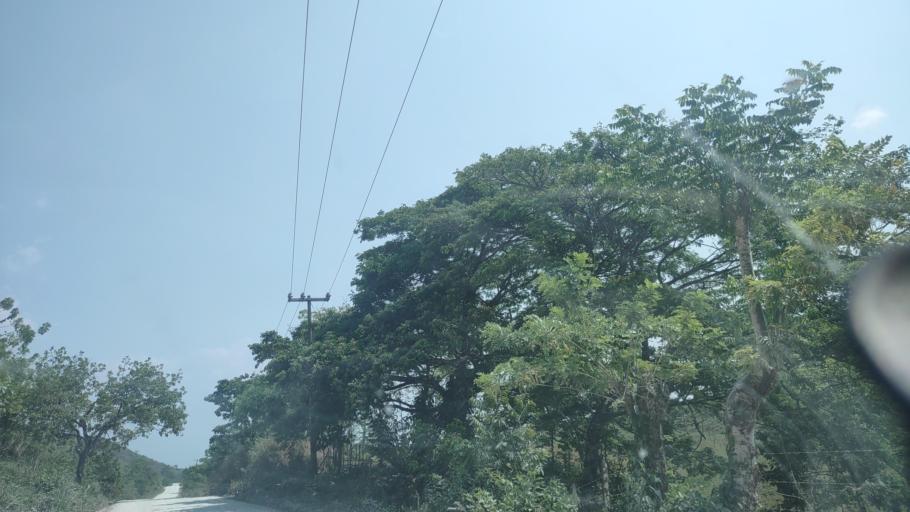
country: MX
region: Tabasco
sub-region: Huimanguillo
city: Francisco Rueda
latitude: 17.5744
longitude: -93.8890
